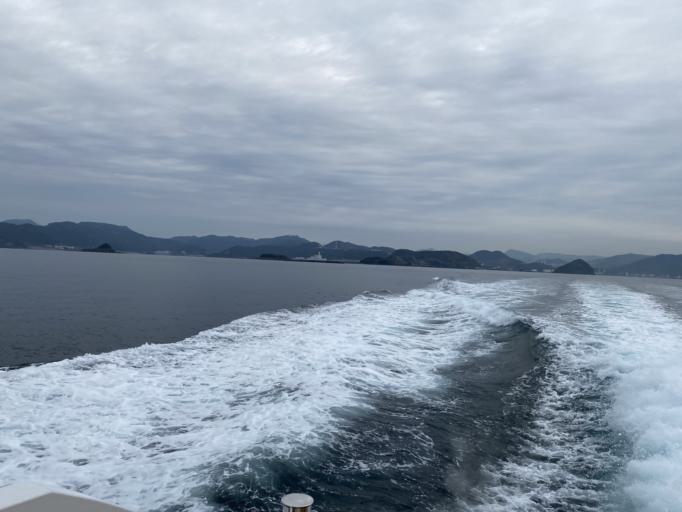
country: JP
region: Nagasaki
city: Nagasaki-shi
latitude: 32.7062
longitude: 129.7996
